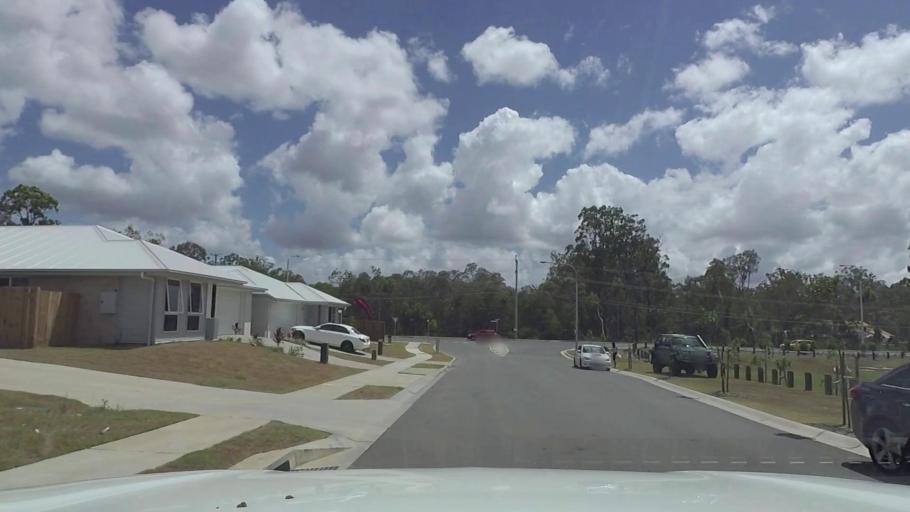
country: AU
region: Queensland
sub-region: Logan
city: Logan Reserve
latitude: -27.7073
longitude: 153.0792
